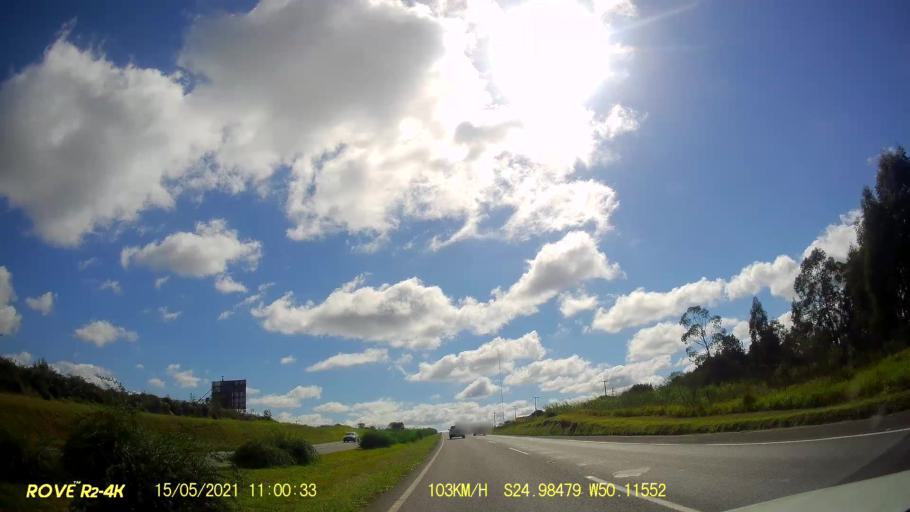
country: BR
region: Parana
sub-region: Carambei
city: Carambei
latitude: -24.9850
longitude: -50.1156
